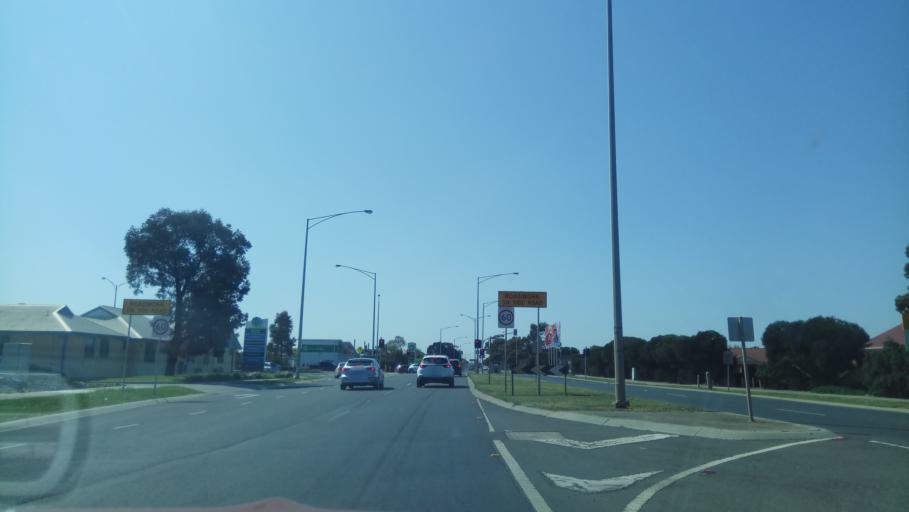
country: AU
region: Victoria
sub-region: Wyndham
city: Point Cook
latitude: -37.8881
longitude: 144.7557
